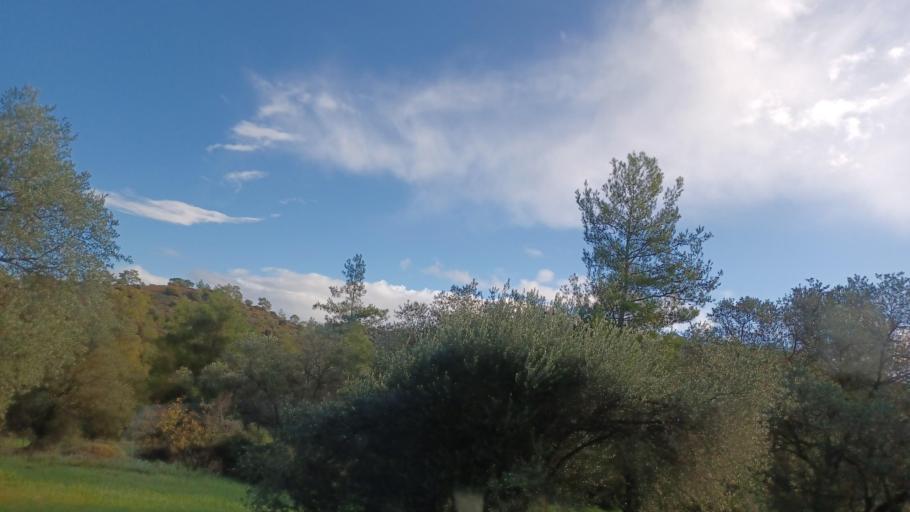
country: CY
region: Lefkosia
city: Lythrodontas
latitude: 34.9287
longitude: 33.2980
